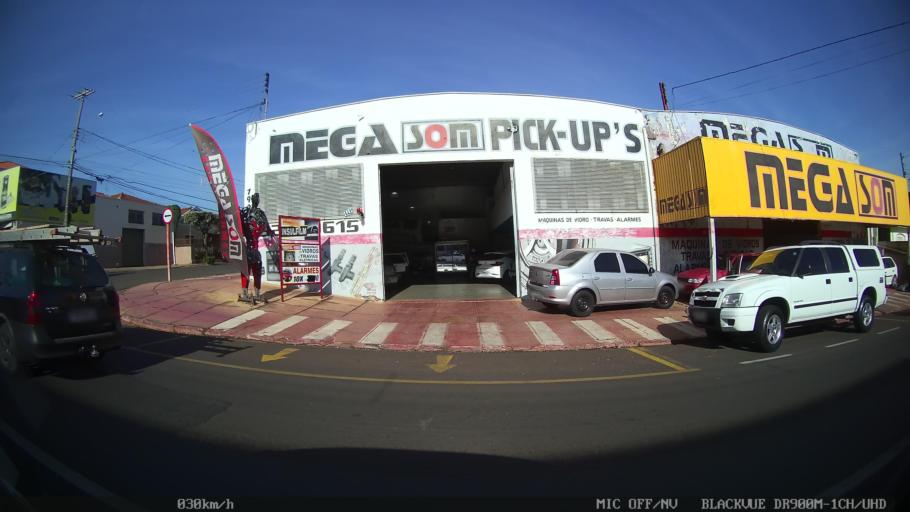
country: BR
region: Sao Paulo
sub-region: Sao Jose Do Rio Preto
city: Sao Jose do Rio Preto
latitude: -20.7973
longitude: -49.3659
